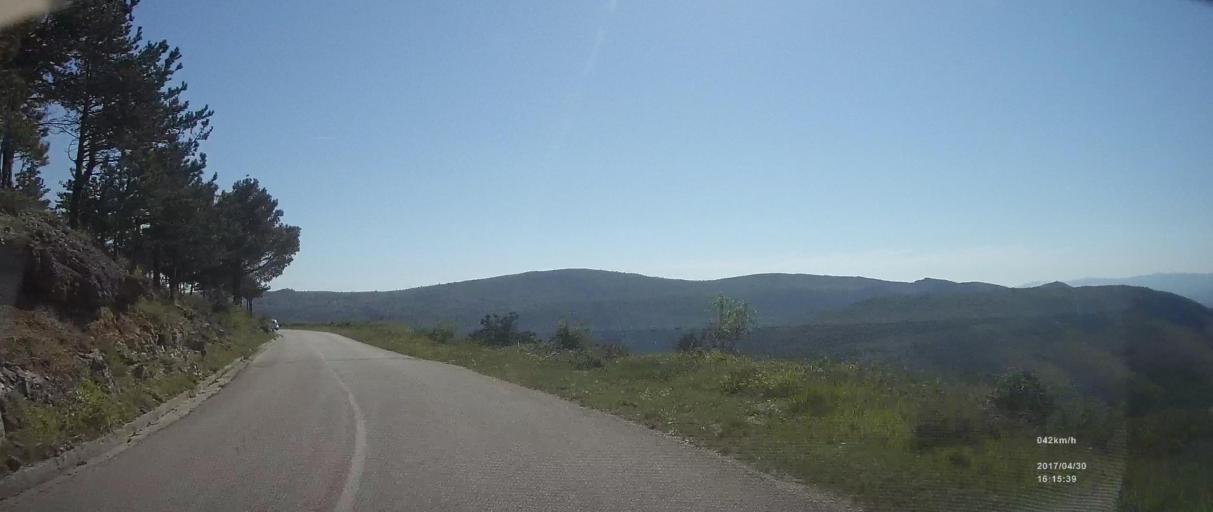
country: HR
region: Splitsko-Dalmatinska
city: Srinjine
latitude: 43.5068
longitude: 16.6056
